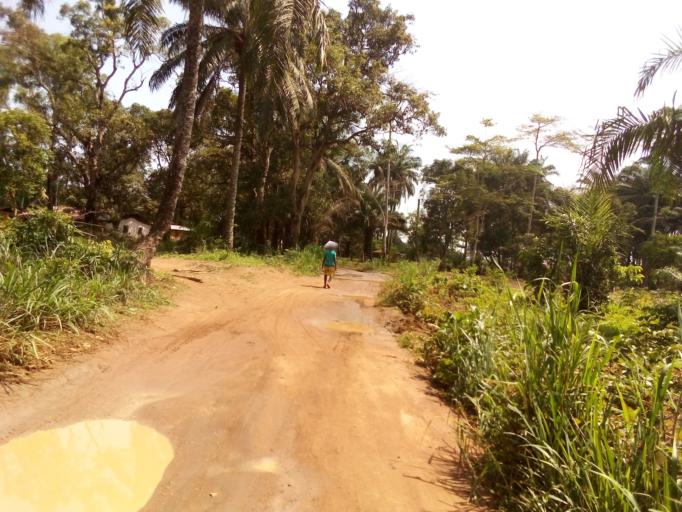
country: SL
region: Western Area
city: Waterloo
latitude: 8.3386
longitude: -13.0076
